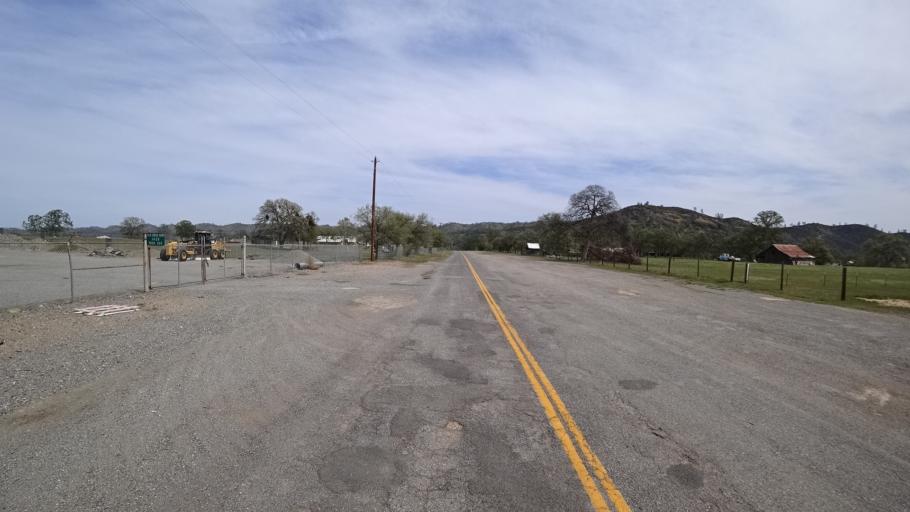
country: US
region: California
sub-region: Glenn County
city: Willows
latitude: 39.6064
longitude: -122.5445
